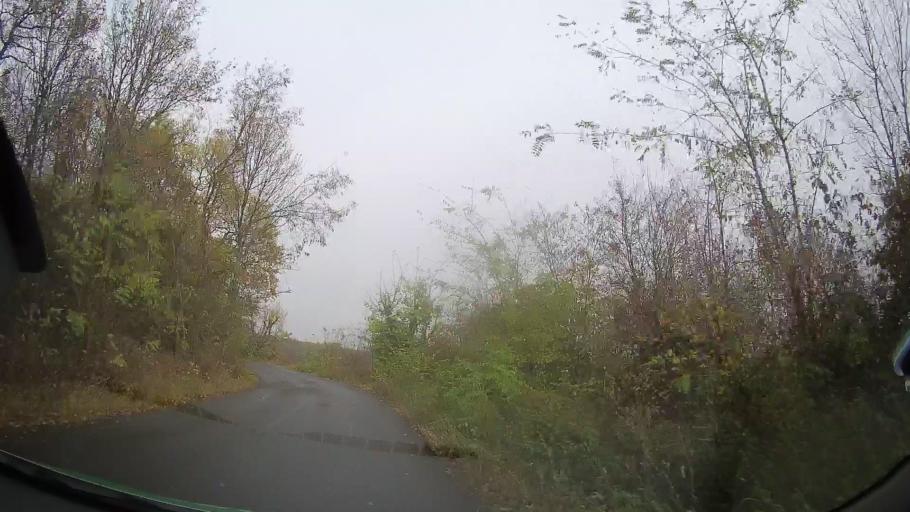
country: RO
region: Prahova
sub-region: Comuna Balta Doamnei
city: Balta Doamnei
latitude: 44.7538
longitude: 26.1282
